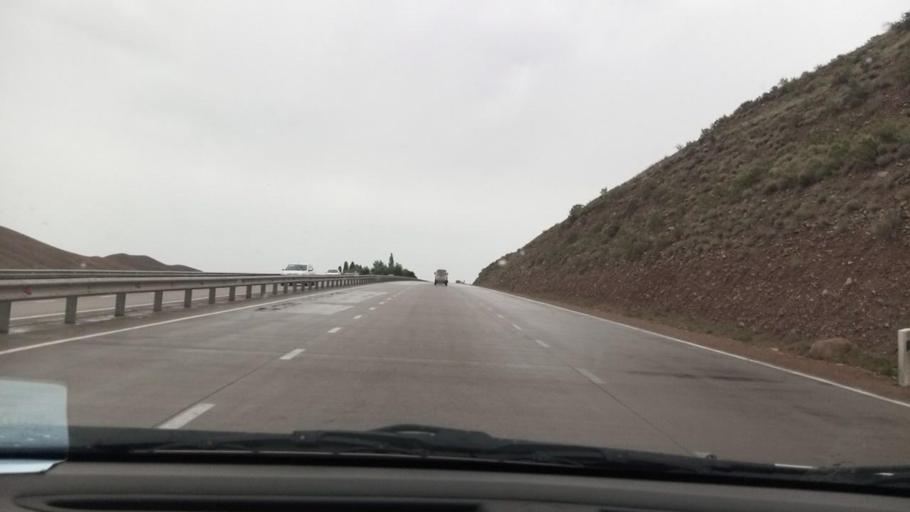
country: UZ
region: Namangan
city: Pop Shahri
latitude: 40.9434
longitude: 70.6865
